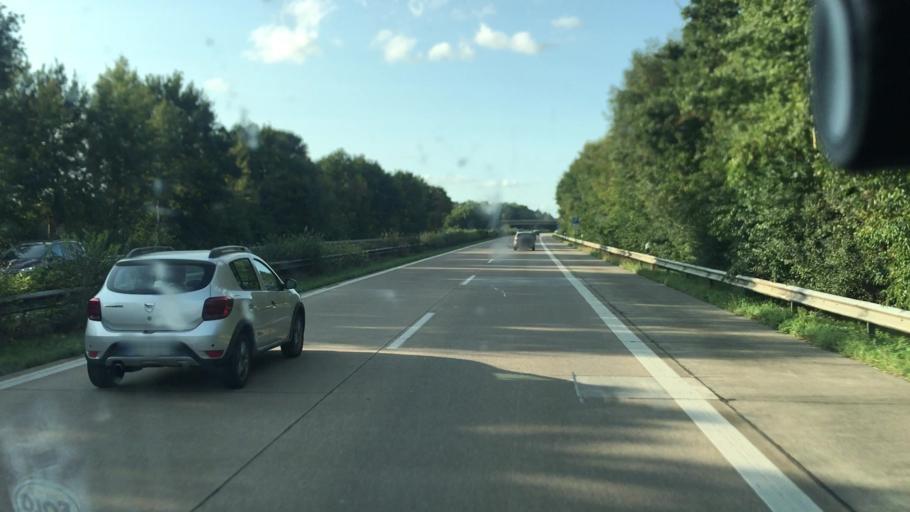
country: DE
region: Lower Saxony
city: Rastede
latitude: 53.2652
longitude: 8.1646
